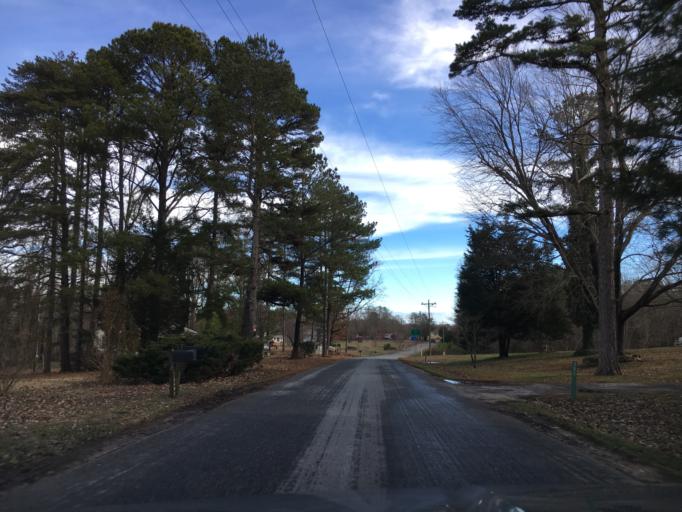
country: US
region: Virginia
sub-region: Nottoway County
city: Crewe
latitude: 37.2379
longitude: -78.2364
